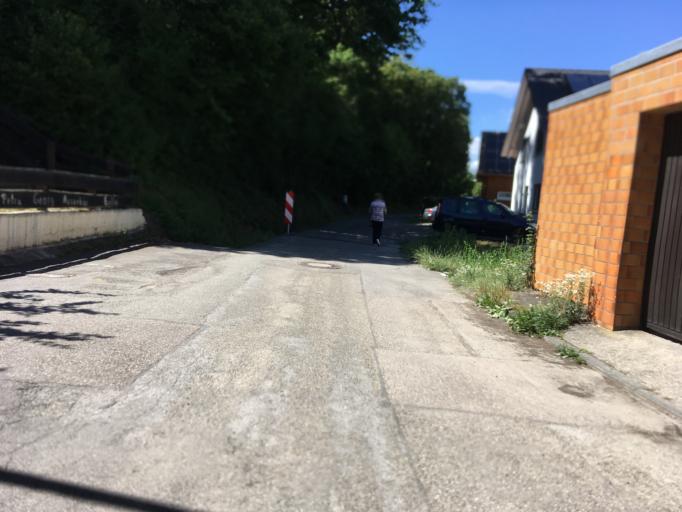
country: DE
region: Baden-Wuerttemberg
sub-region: Karlsruhe Region
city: Muhlacker
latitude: 48.9327
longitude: 8.8418
